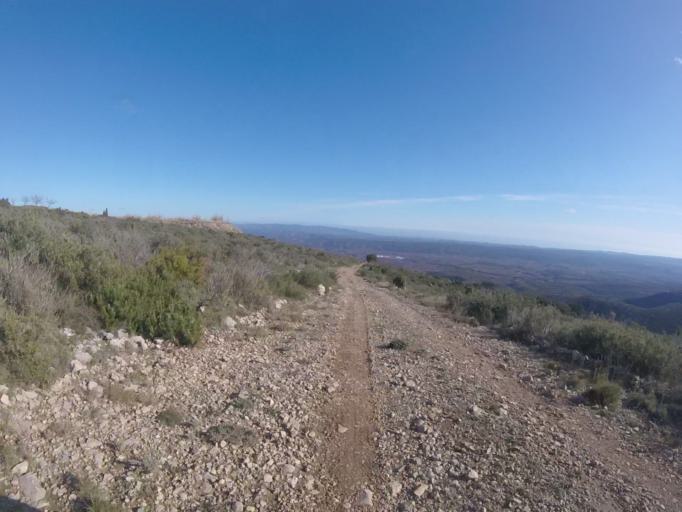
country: ES
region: Valencia
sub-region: Provincia de Castello
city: Sarratella
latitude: 40.3007
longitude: 0.0340
